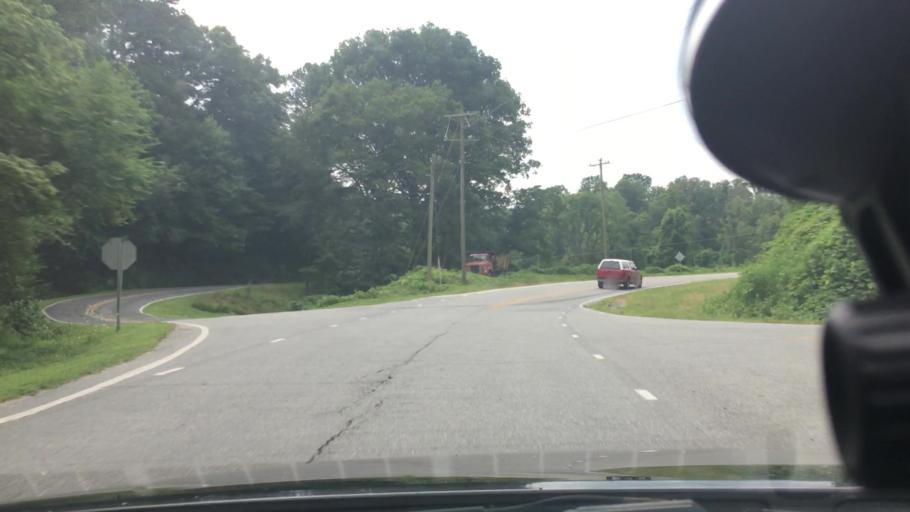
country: US
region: North Carolina
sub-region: McDowell County
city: West Marion
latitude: 35.6545
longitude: -82.0152
